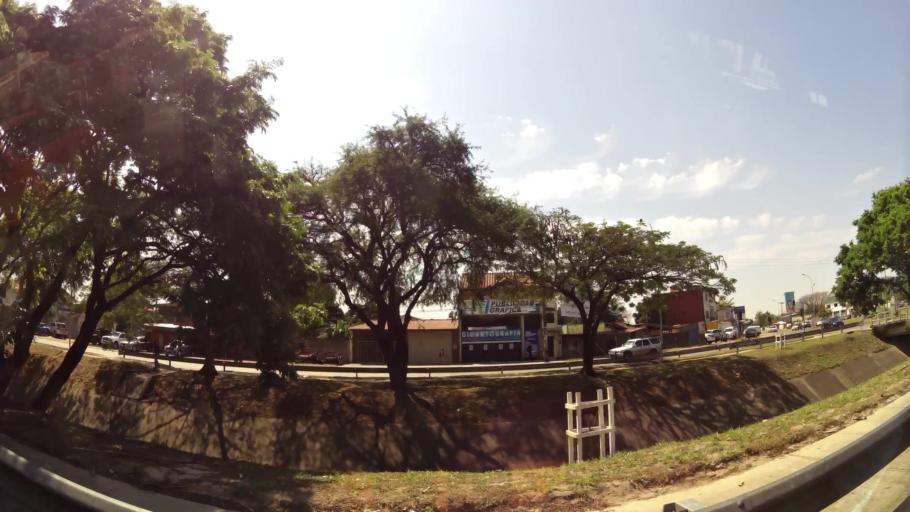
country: BO
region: Santa Cruz
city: Santa Cruz de la Sierra
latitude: -17.7517
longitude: -63.1648
